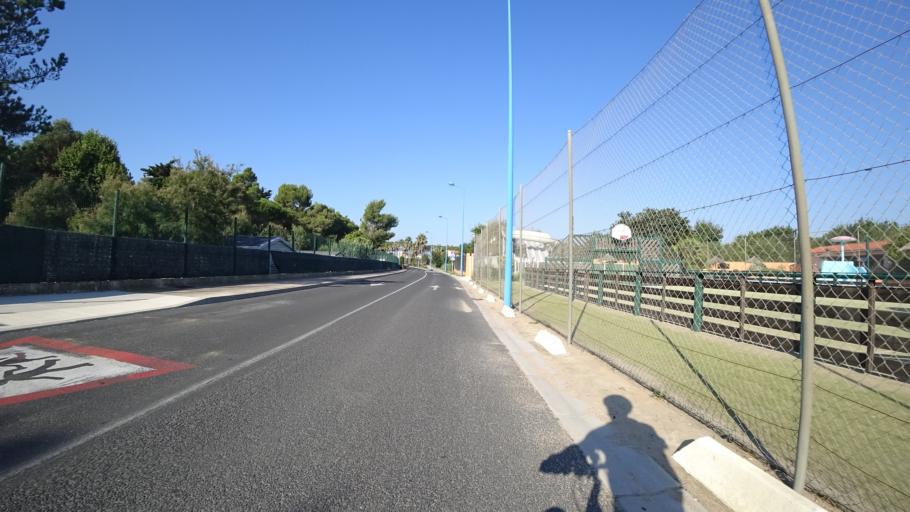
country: FR
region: Languedoc-Roussillon
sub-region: Departement des Pyrenees-Orientales
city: Canet-en-Roussillon
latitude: 42.7011
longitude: 2.9982
